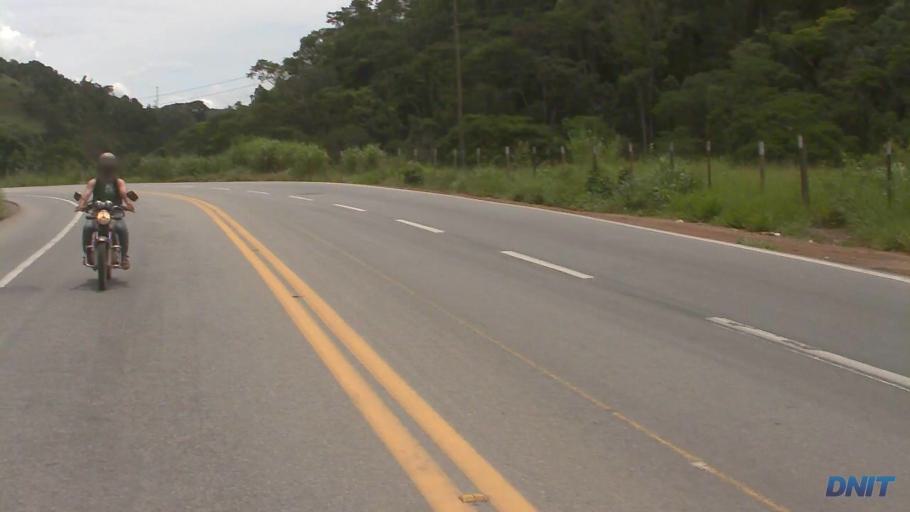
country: BR
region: Minas Gerais
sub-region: Timoteo
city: Timoteo
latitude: -19.6200
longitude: -42.8447
